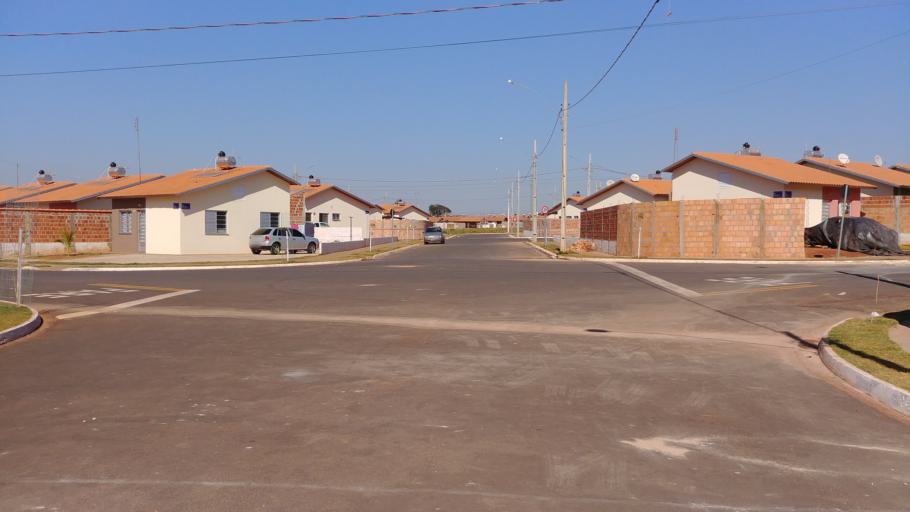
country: BR
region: Sao Paulo
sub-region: Paraguacu Paulista
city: Paraguacu Paulista
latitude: -22.4428
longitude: -50.5883
